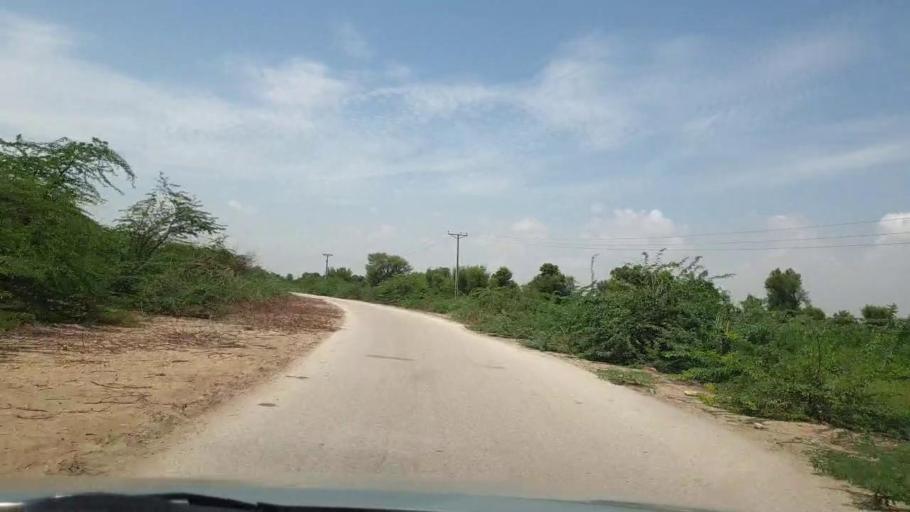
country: PK
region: Sindh
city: Bozdar
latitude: 27.0354
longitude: 68.9596
